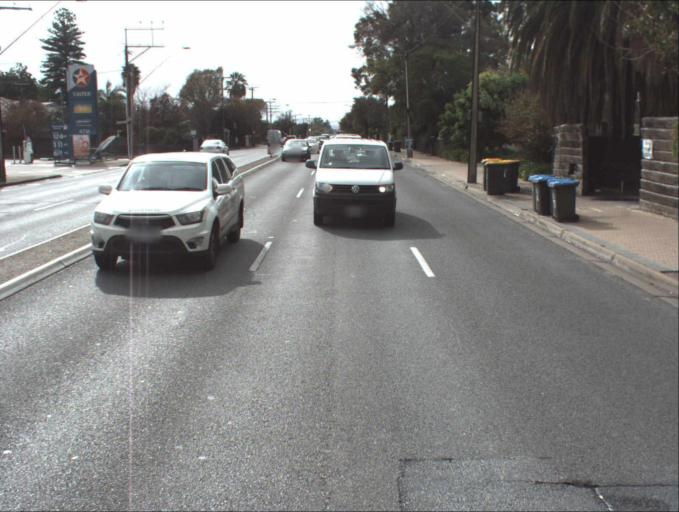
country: AU
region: South Australia
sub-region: Port Adelaide Enfield
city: Klemzig
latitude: -34.8870
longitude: 138.6164
